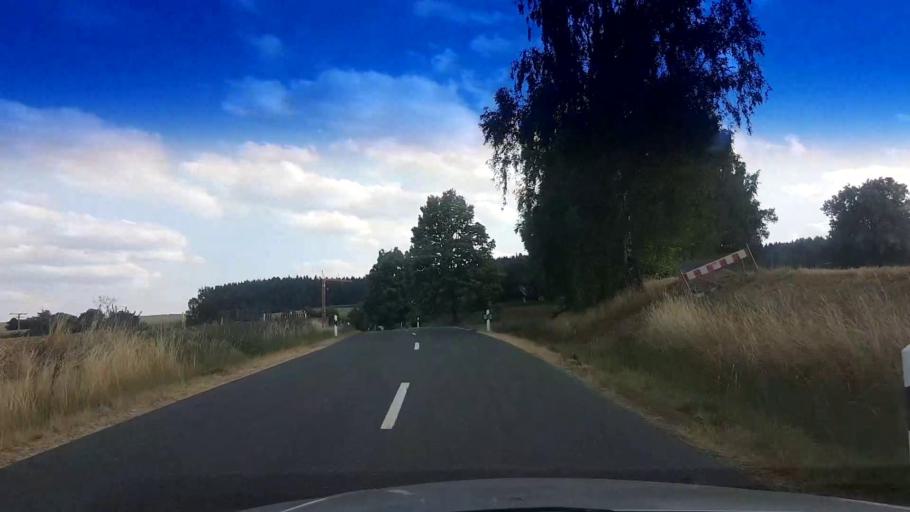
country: DE
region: Bavaria
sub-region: Upper Palatinate
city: Waldsassen
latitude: 50.0180
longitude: 12.3586
